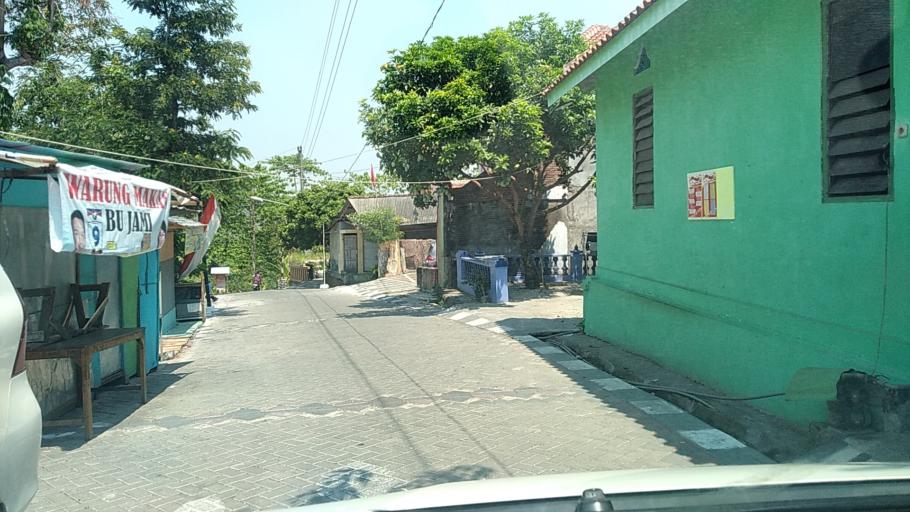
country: ID
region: Central Java
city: Semarang
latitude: -7.0341
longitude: 110.4076
